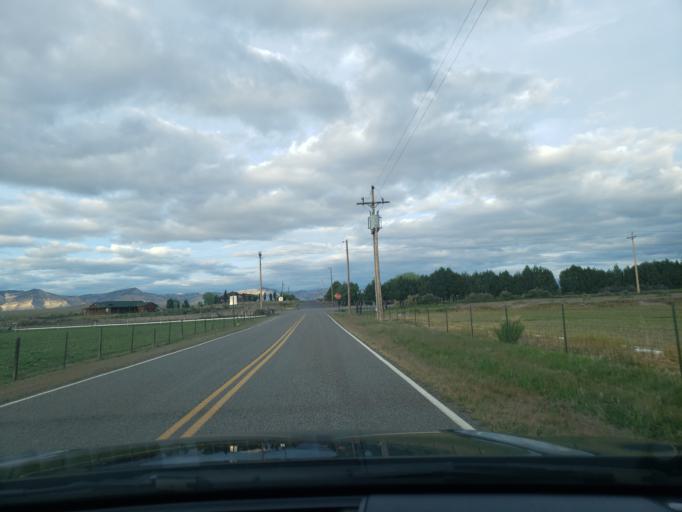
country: US
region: Colorado
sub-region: Mesa County
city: Fruita
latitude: 39.2221
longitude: -108.7023
